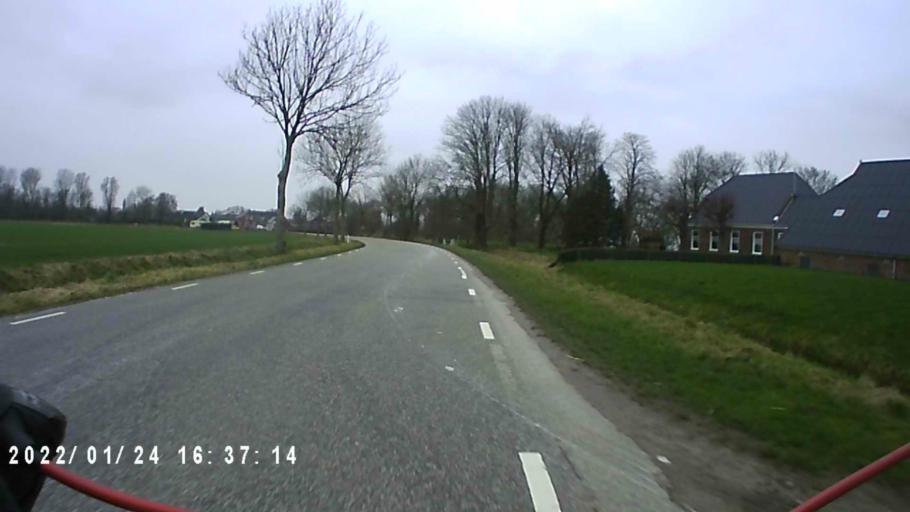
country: NL
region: Groningen
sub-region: Gemeente De Marne
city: Ulrum
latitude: 53.3857
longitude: 6.4105
